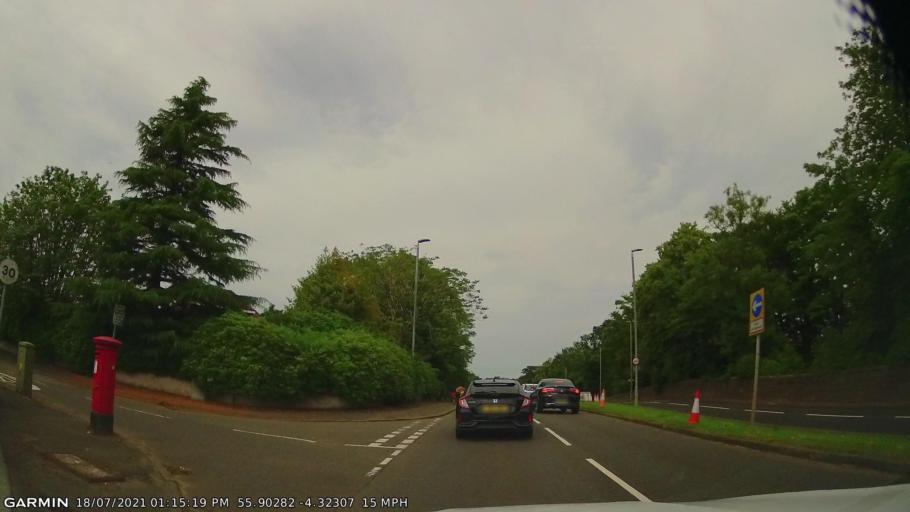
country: GB
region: Scotland
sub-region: East Dunbartonshire
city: Bearsden
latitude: 55.9028
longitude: -4.3231
